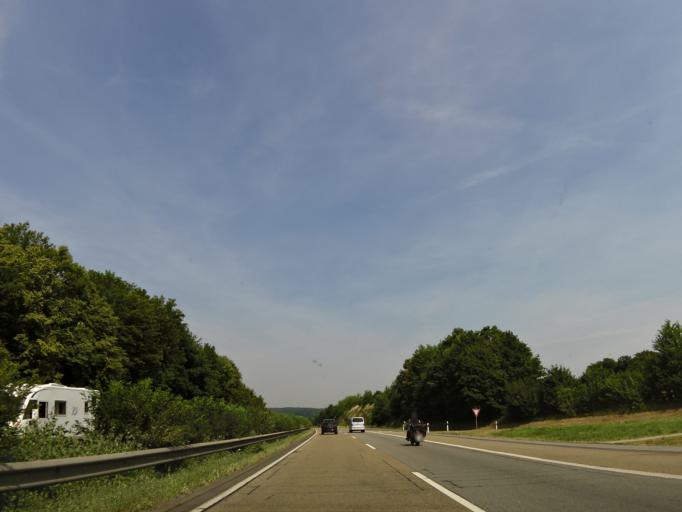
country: DE
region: Rheinland-Pfalz
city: Niederzissen
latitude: 50.4690
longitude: 7.2314
